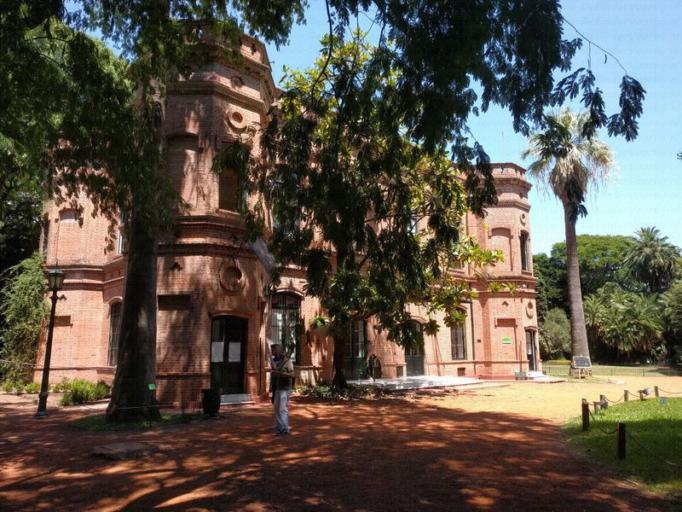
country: AR
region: Buenos Aires F.D.
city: Colegiales
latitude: -34.5823
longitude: -58.4185
